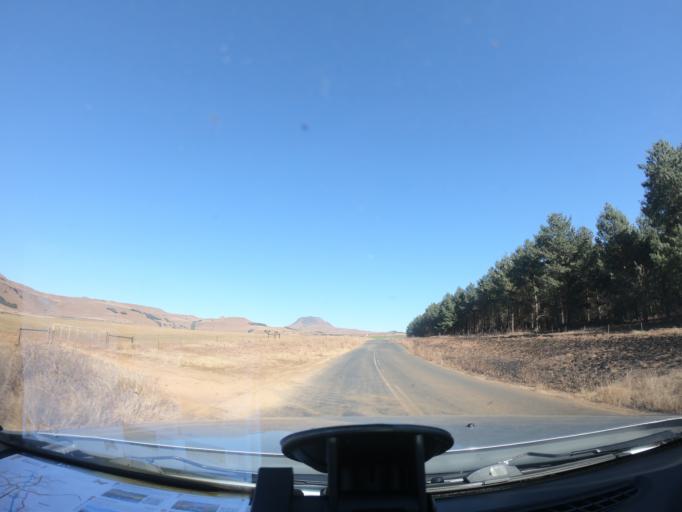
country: ZA
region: KwaZulu-Natal
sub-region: uMgungundlovu District Municipality
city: Mooirivier
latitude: -29.3326
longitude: 29.8183
